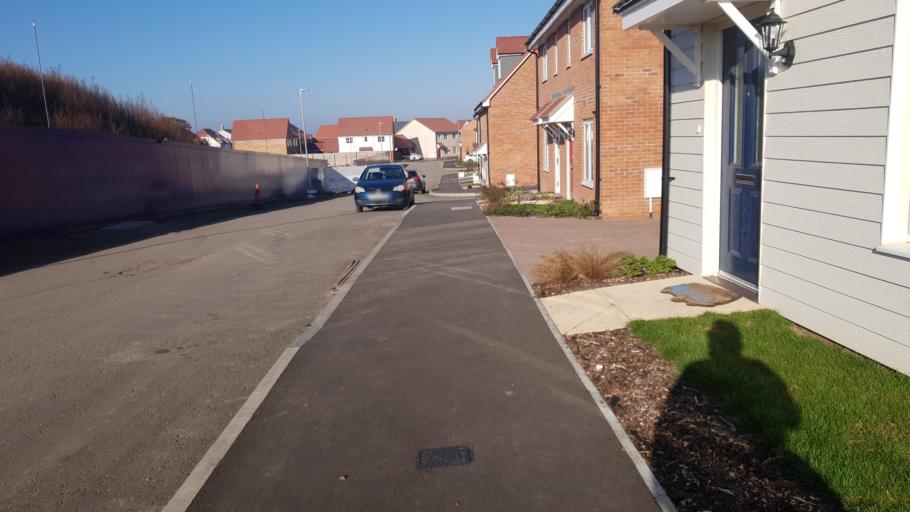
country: GB
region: England
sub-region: Essex
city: Walton-on-the-Naze
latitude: 51.8521
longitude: 1.2649
